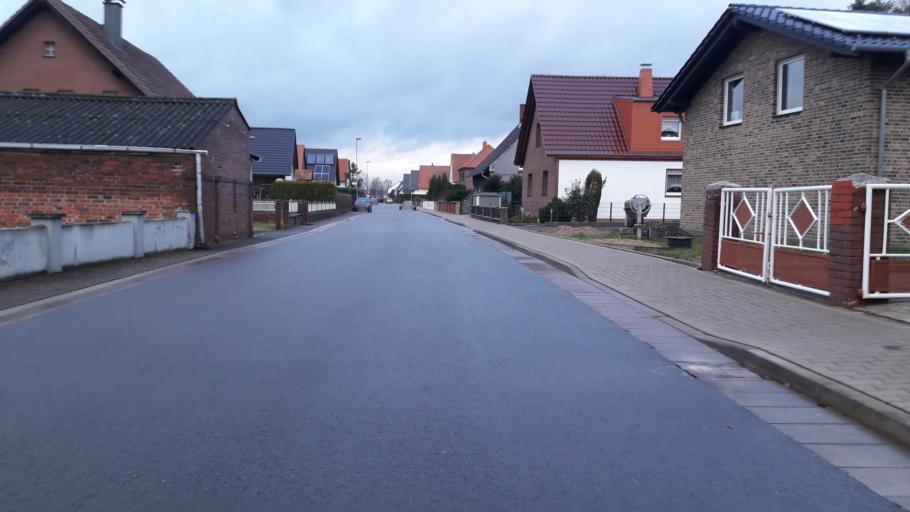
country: DE
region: North Rhine-Westphalia
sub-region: Regierungsbezirk Detmold
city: Minden
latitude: 52.3086
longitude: 8.9303
